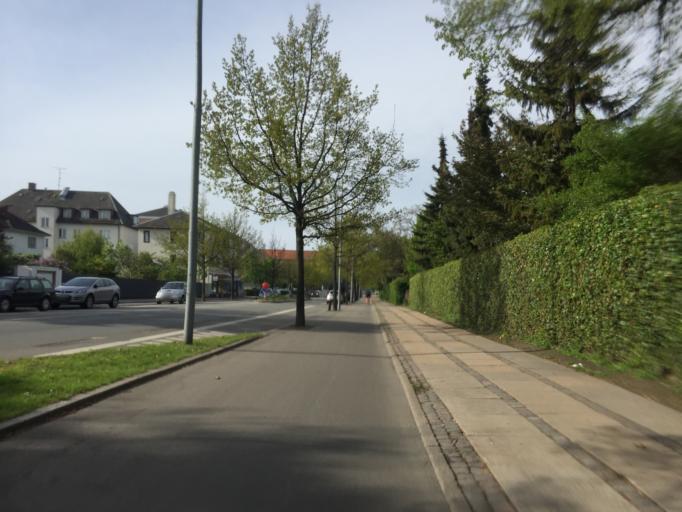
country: DK
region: Capital Region
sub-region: Frederiksberg Kommune
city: Frederiksberg
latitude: 55.6864
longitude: 12.5143
